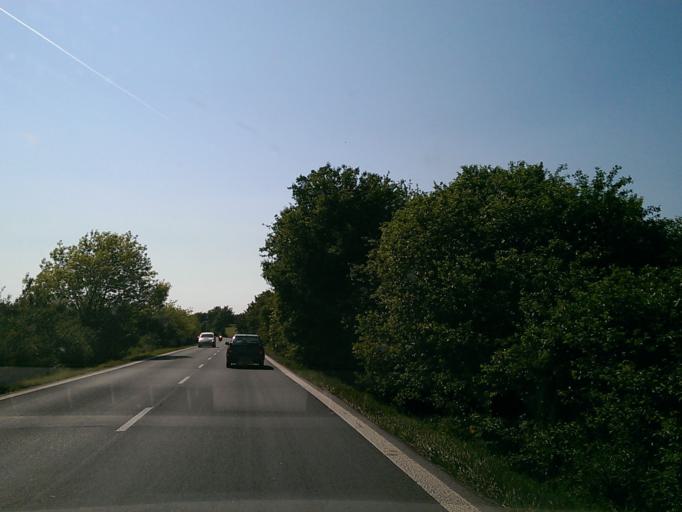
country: CZ
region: Liberecky
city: Rovensko pod Troskami
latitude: 50.5065
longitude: 15.2785
